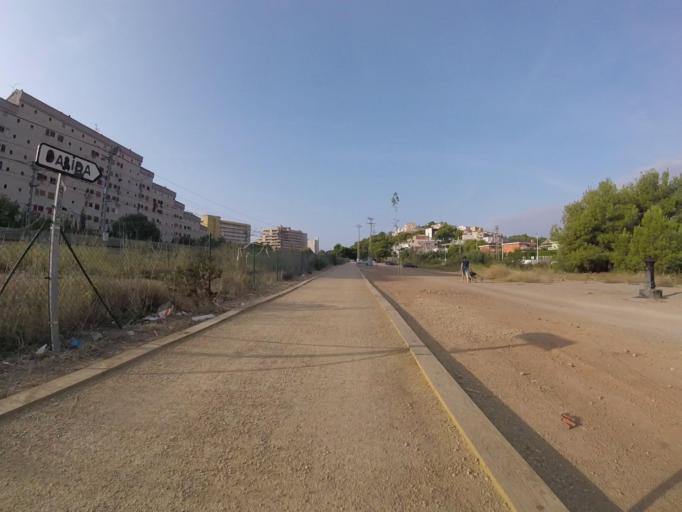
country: ES
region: Valencia
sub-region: Provincia de Castello
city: Orpesa/Oropesa del Mar
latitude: 40.0850
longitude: 0.1371
